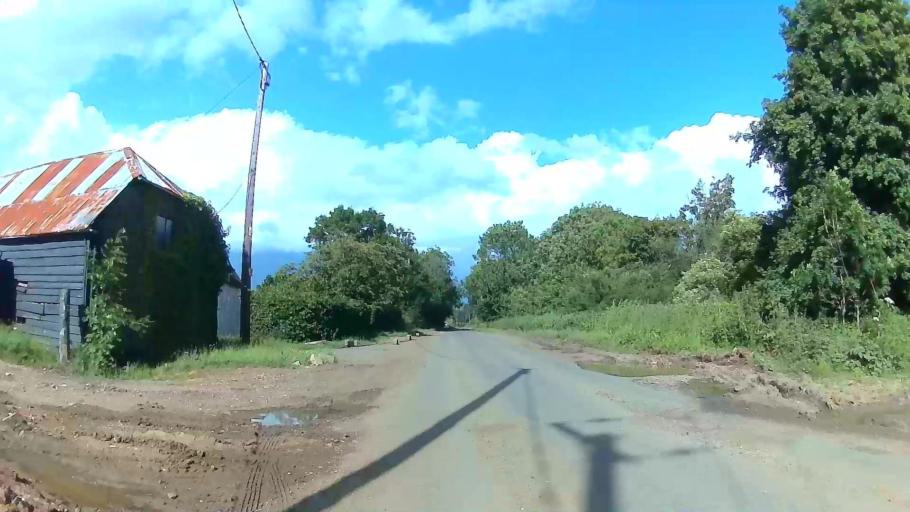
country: GB
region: England
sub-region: Essex
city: Kelvedon Hatch
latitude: 51.6493
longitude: 0.2442
